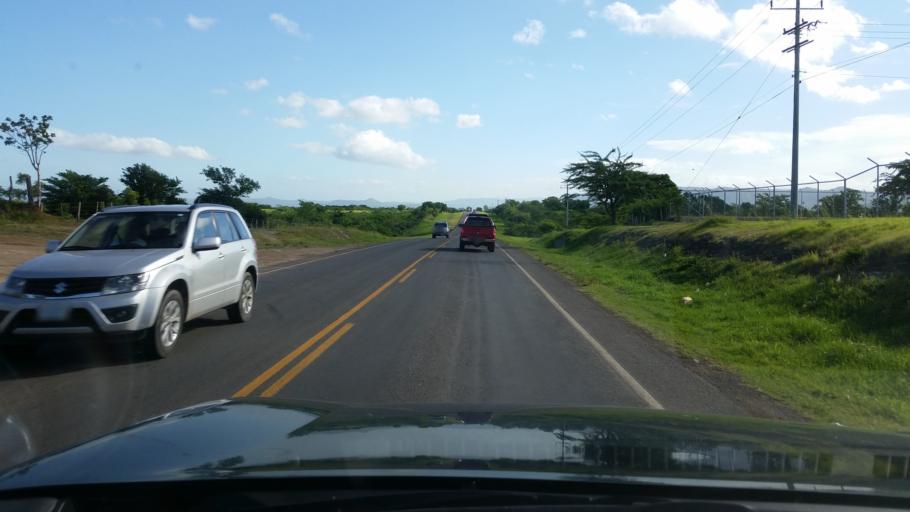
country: NI
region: Managua
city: Tipitapa
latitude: 12.3168
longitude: -86.0538
